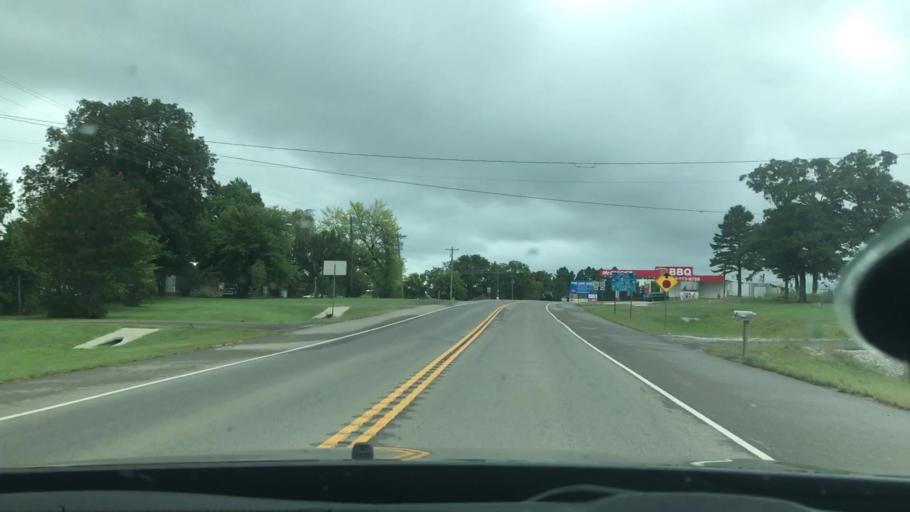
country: US
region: Oklahoma
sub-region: Sequoyah County
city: Vian
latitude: 35.6075
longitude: -94.9763
